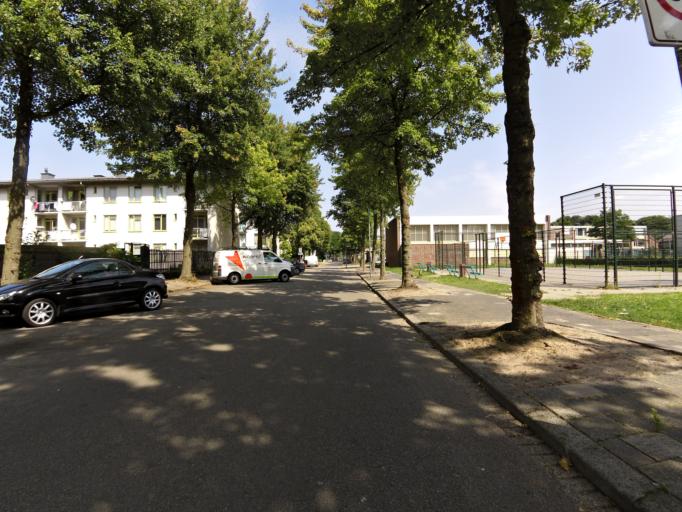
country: NL
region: South Holland
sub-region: Gemeente Dordrecht
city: Dordrecht
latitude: 51.7984
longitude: 4.6671
